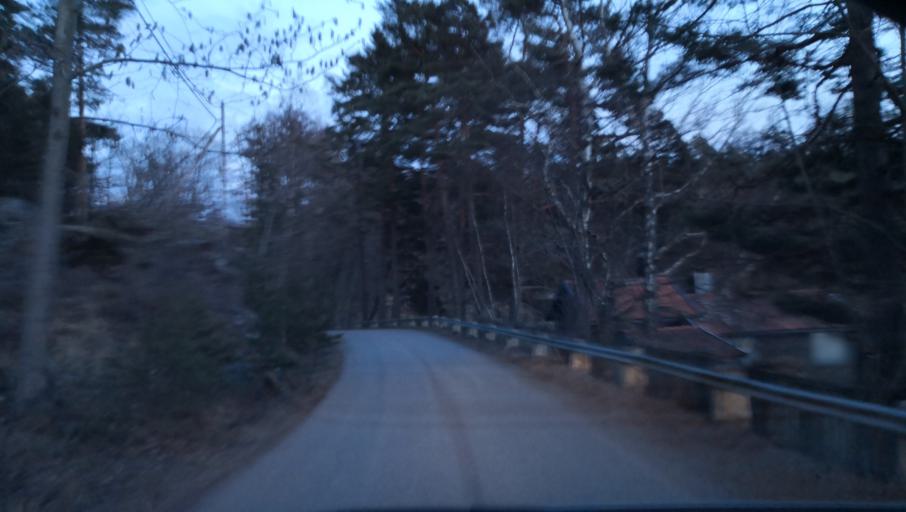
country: SE
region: Stockholm
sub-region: Nacka Kommun
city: Boo
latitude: 59.3239
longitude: 18.3301
